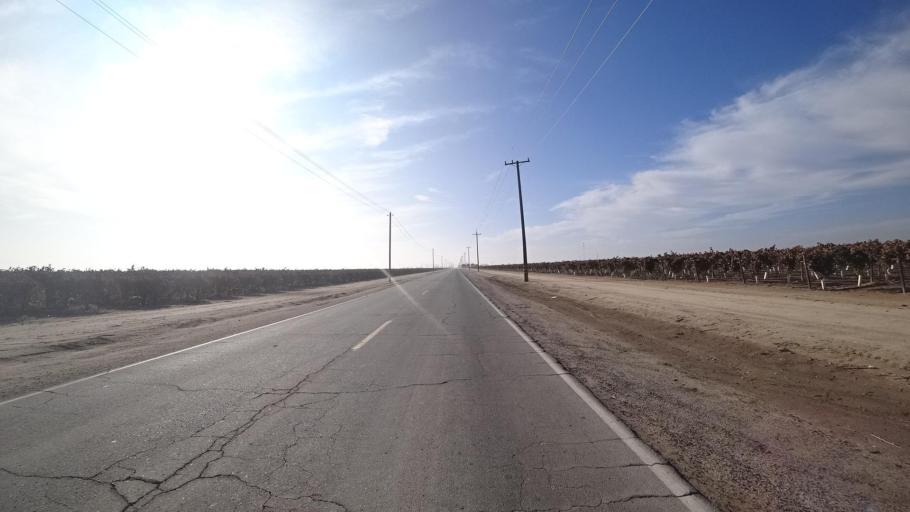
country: US
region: California
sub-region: Kern County
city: McFarland
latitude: 35.6164
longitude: -119.2044
